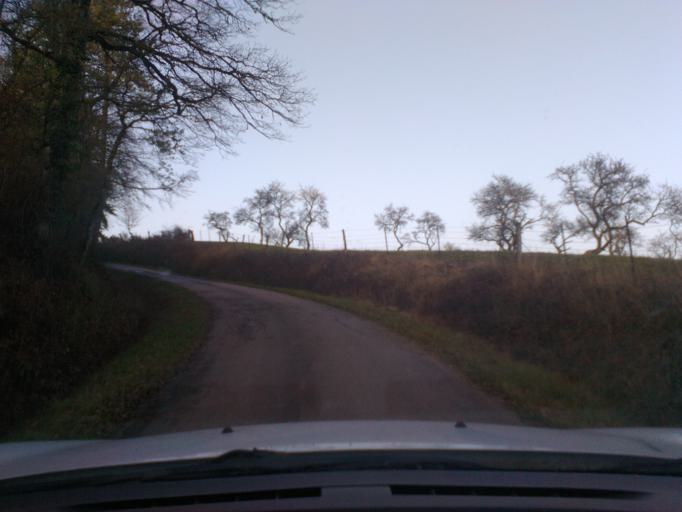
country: FR
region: Lorraine
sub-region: Departement des Vosges
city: Vittel
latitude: 48.2567
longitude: 6.0010
